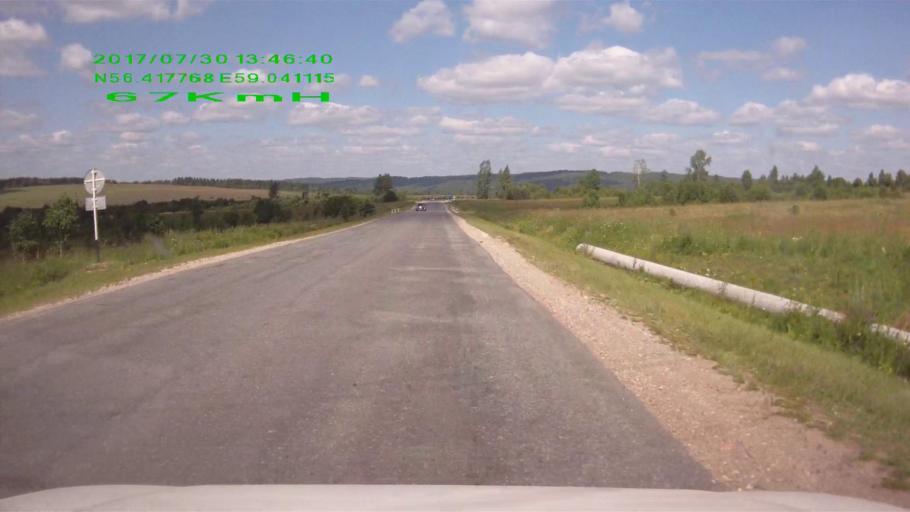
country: RU
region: Sverdlovsk
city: Mikhaylovsk
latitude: 56.4180
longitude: 59.0411
